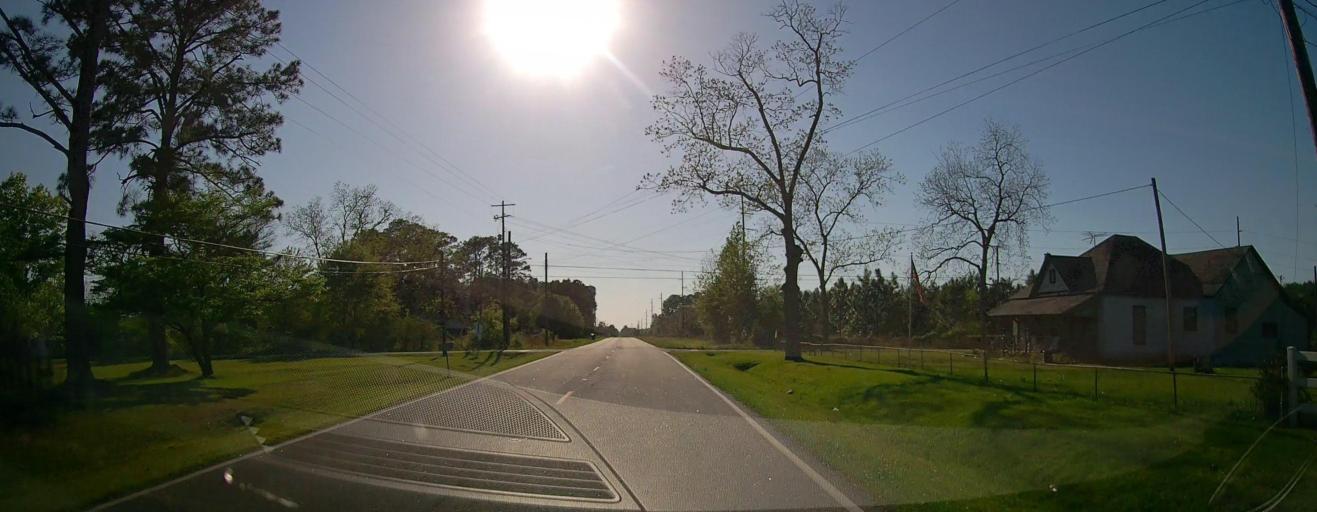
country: US
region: Georgia
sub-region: Ben Hill County
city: Fitzgerald
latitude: 31.7436
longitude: -83.2518
